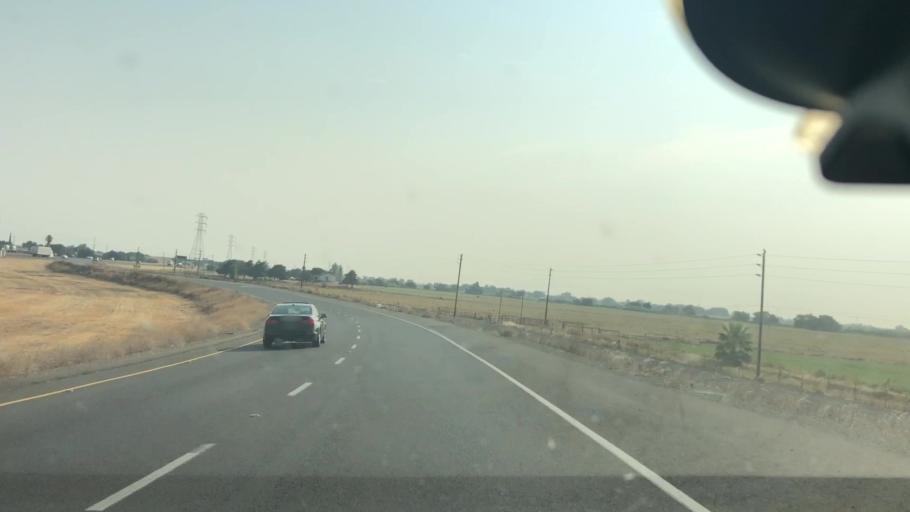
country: US
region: California
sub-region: San Joaquin County
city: Tracy
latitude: 37.7595
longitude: -121.3402
